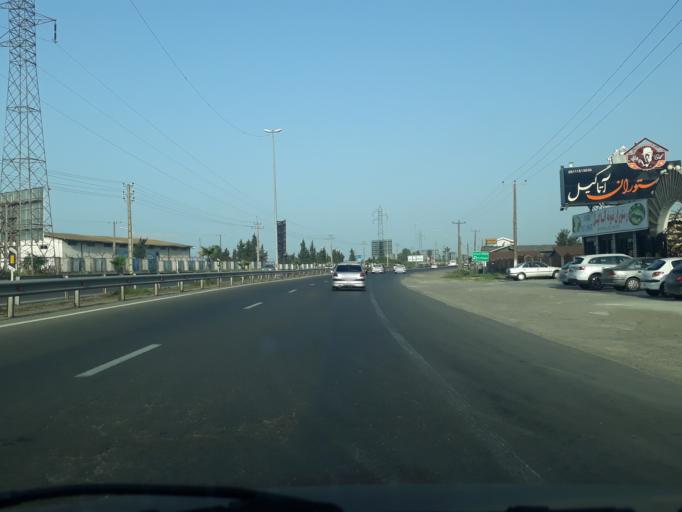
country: IR
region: Gilan
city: Bandar-e Anzali
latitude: 37.4601
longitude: 49.5878
